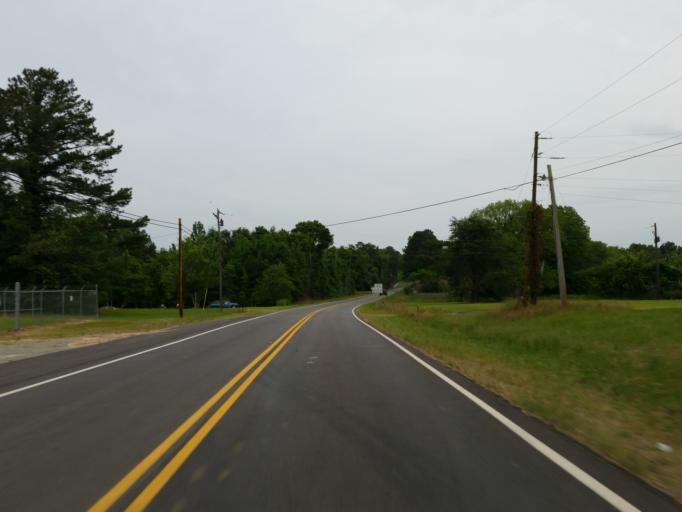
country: US
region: Georgia
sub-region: Dooly County
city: Unadilla
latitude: 32.2759
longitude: -83.7403
